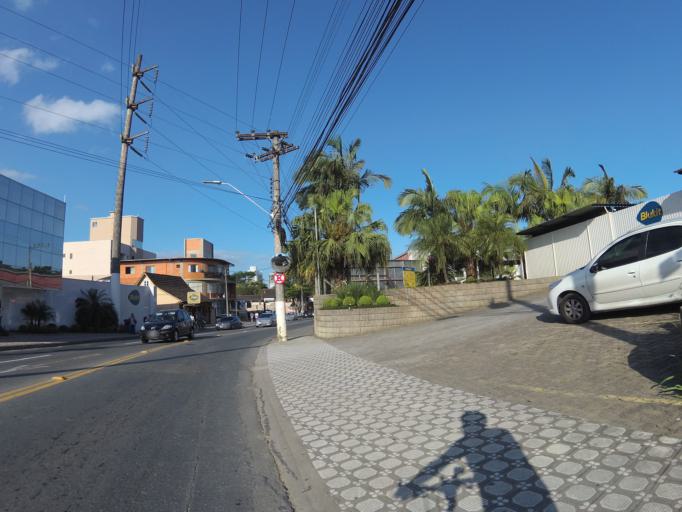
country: BR
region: Santa Catarina
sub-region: Blumenau
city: Blumenau
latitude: -26.9204
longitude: -49.0978
